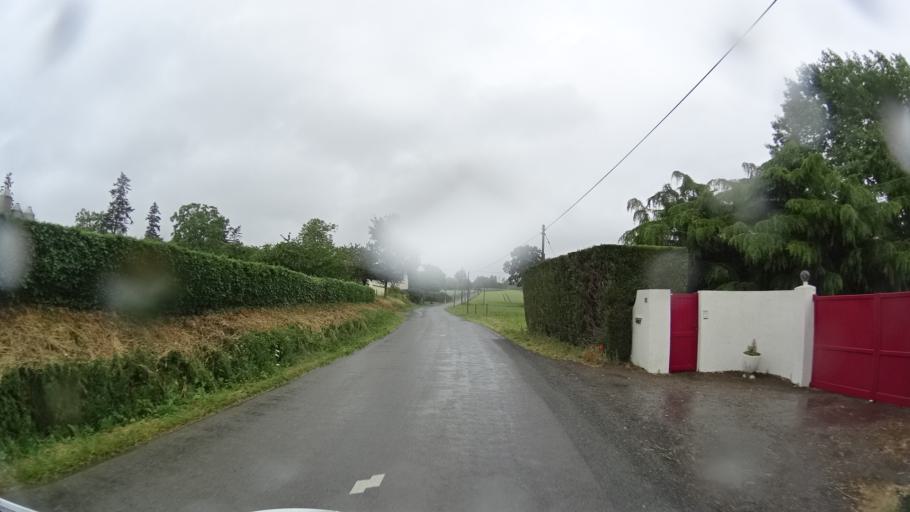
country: FR
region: Brittany
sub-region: Departement d'Ille-et-Vilaine
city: Vern-sur-Seiche
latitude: 48.0394
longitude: -1.6260
